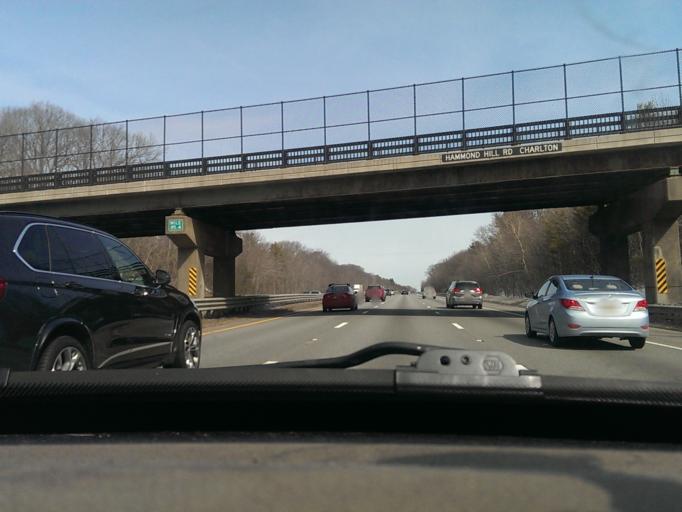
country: US
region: Massachusetts
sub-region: Worcester County
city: Charlton
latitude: 42.1675
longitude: -71.9375
